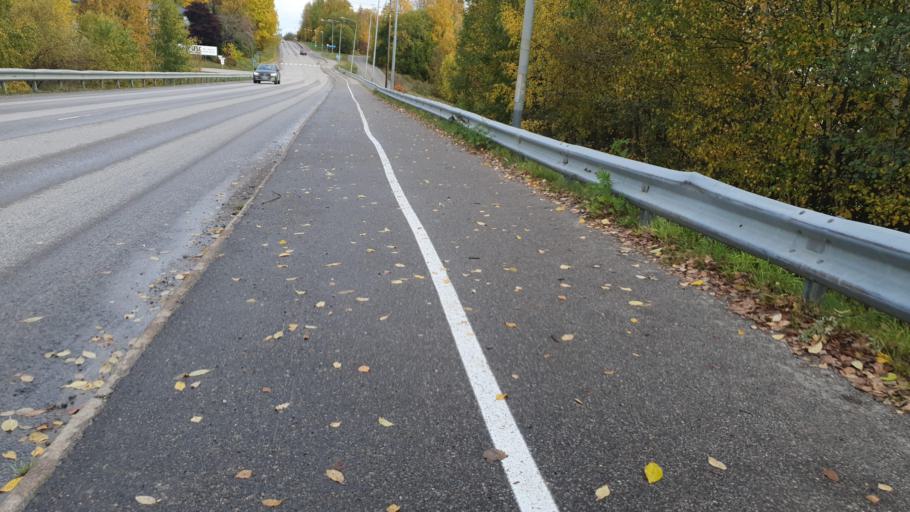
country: SE
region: Vaesternorrland
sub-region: Sundsvalls Kommun
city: Sundsbruk
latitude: 62.4511
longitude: 17.3461
